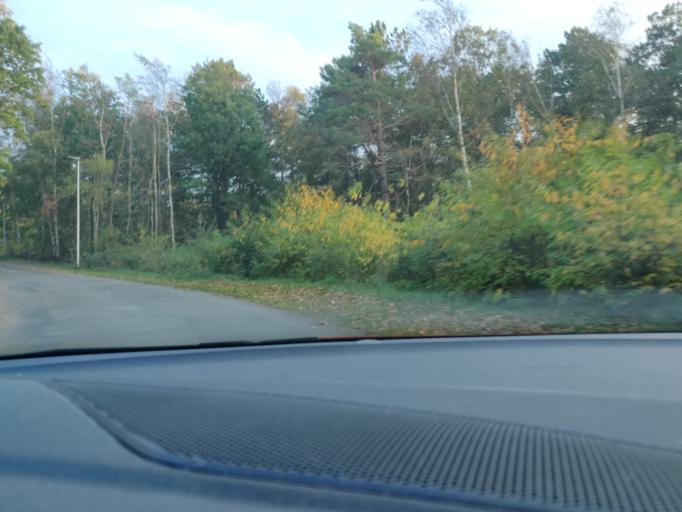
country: DE
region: Lower Saxony
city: Nordholz
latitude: 53.8641
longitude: 8.6006
